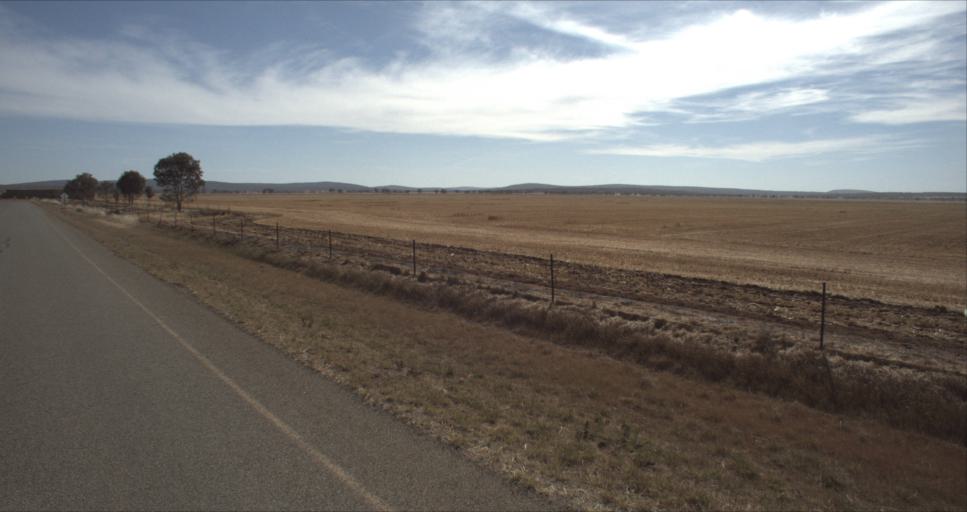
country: AU
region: New South Wales
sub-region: Leeton
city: Leeton
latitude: -34.5627
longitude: 146.4814
